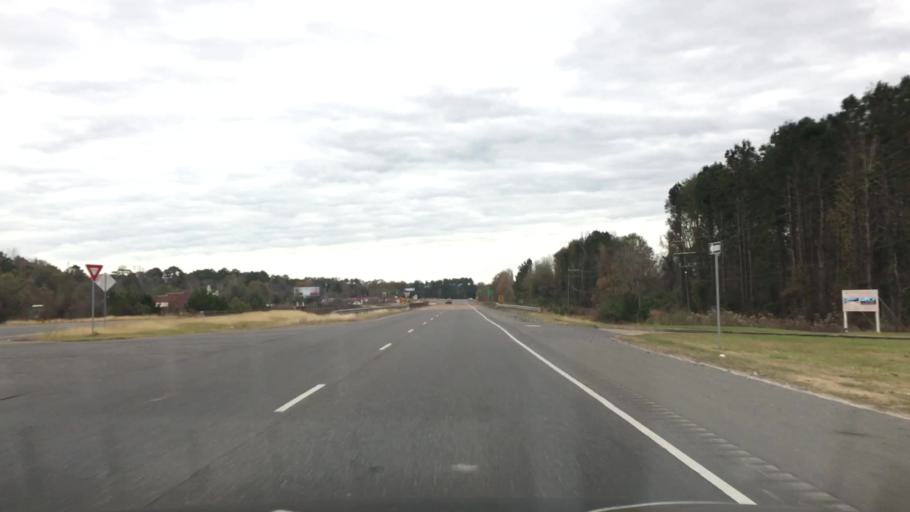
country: US
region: Louisiana
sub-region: Vernon Parish
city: New Llano
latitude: 31.1091
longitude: -93.2712
